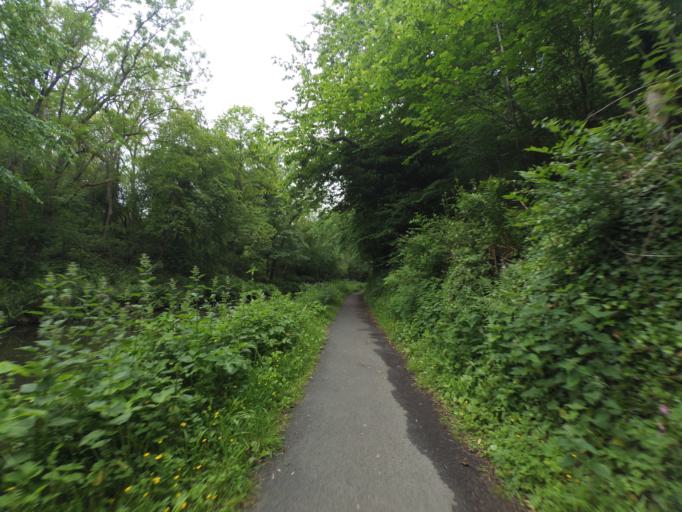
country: GB
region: Scotland
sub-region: Falkirk
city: Polmont
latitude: 55.9651
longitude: -3.6601
